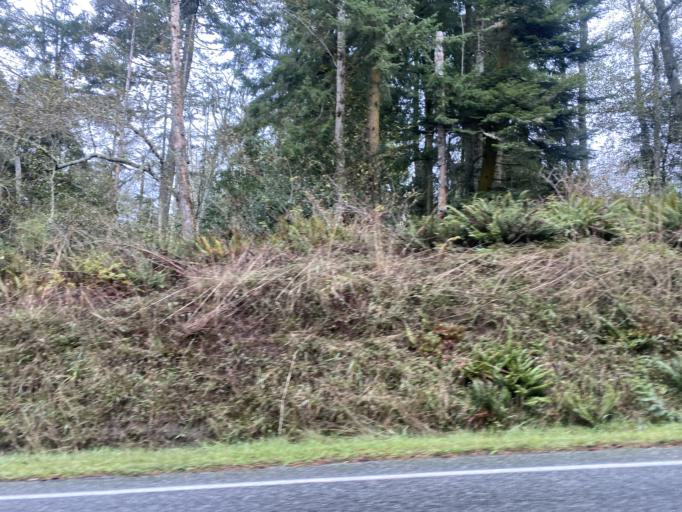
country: US
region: Washington
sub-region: Island County
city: Freeland
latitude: 48.0660
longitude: -122.5002
